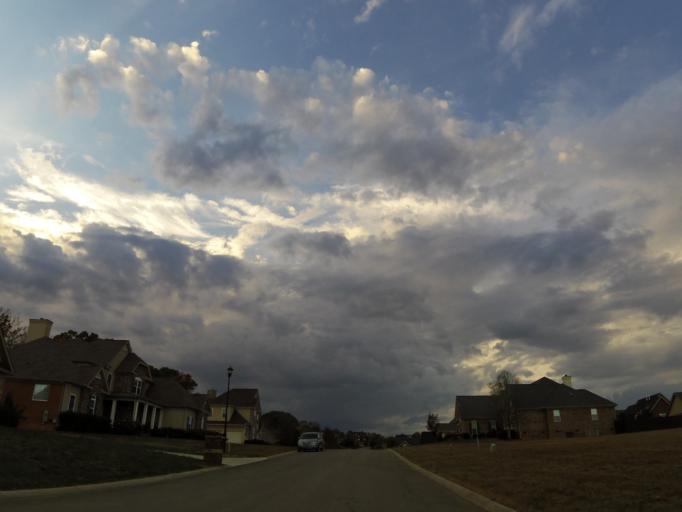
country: US
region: Tennessee
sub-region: Blount County
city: Maryville
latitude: 35.7632
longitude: -84.0257
